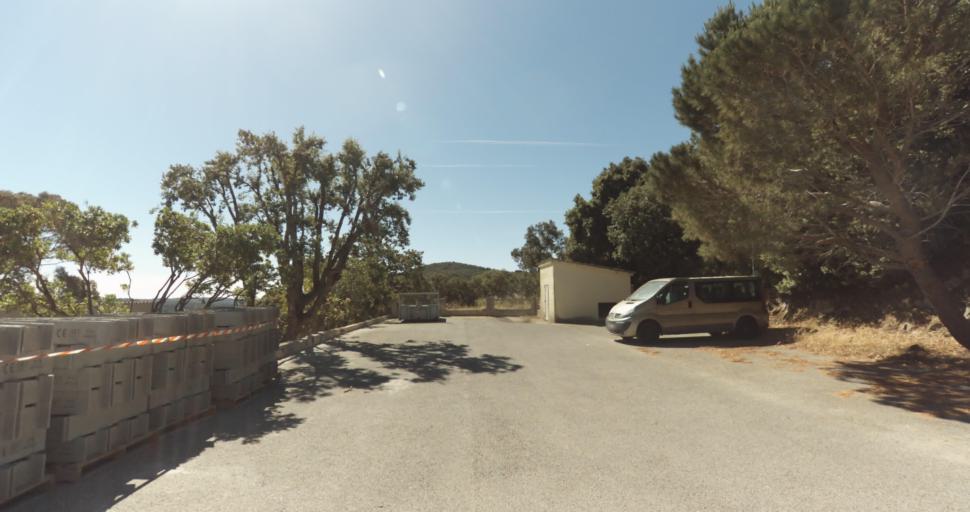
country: FR
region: Provence-Alpes-Cote d'Azur
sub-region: Departement du Var
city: Saint-Tropez
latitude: 43.2587
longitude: 6.6125
